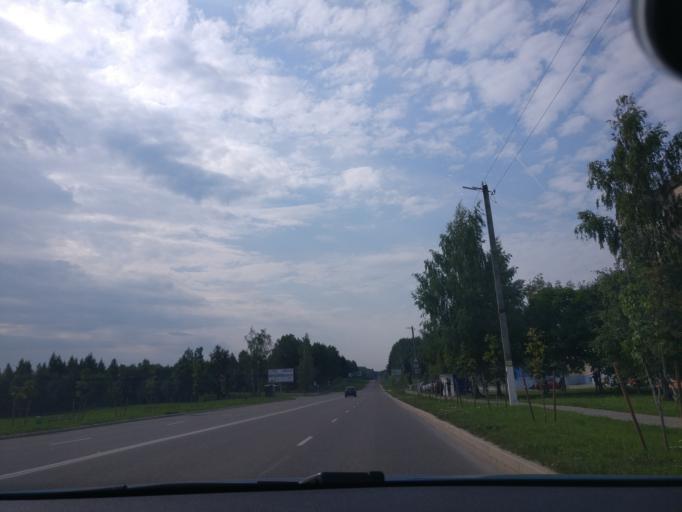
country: BY
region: Minsk
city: Lahoysk
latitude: 54.1928
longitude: 27.8319
